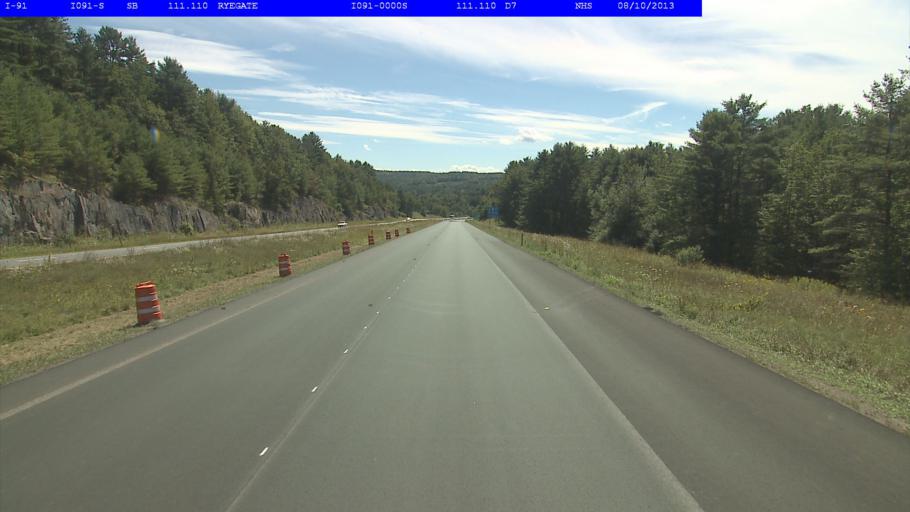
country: US
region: New Hampshire
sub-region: Grafton County
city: Woodsville
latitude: 44.1702
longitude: -72.0830
